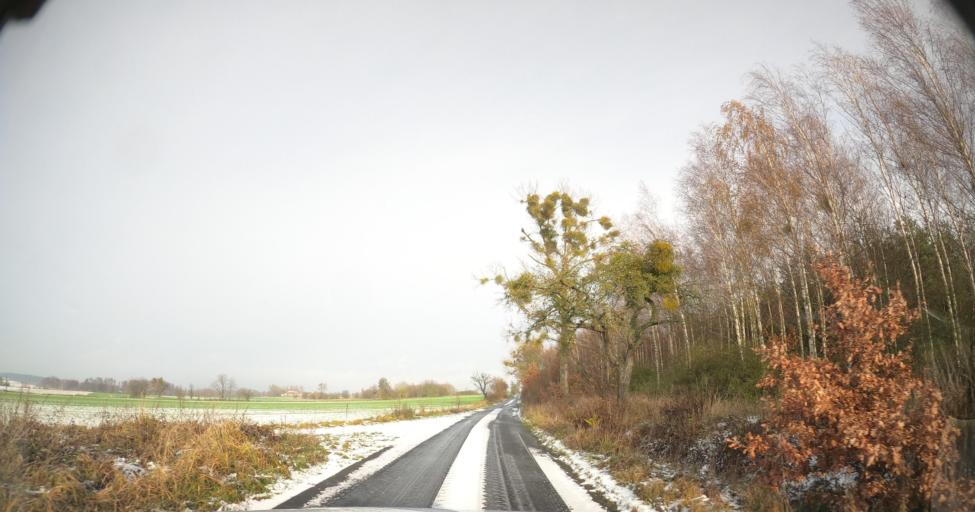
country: PL
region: West Pomeranian Voivodeship
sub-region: Powiat gryfinski
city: Mieszkowice
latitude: 52.7658
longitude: 14.4864
